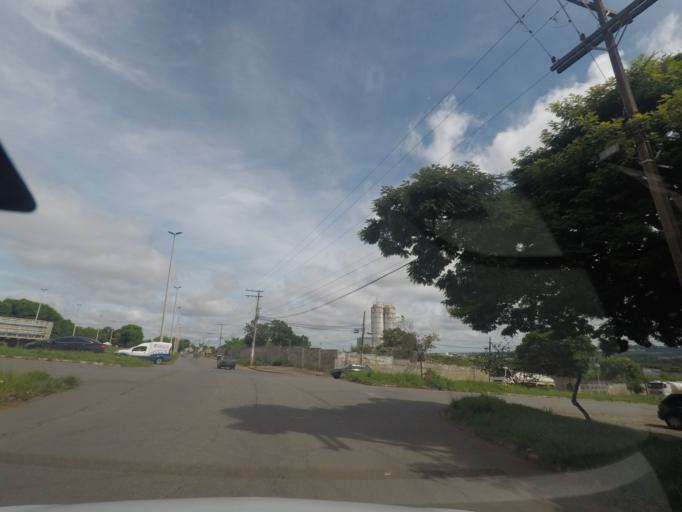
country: BR
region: Goias
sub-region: Goiania
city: Goiania
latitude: -16.6694
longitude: -49.2082
